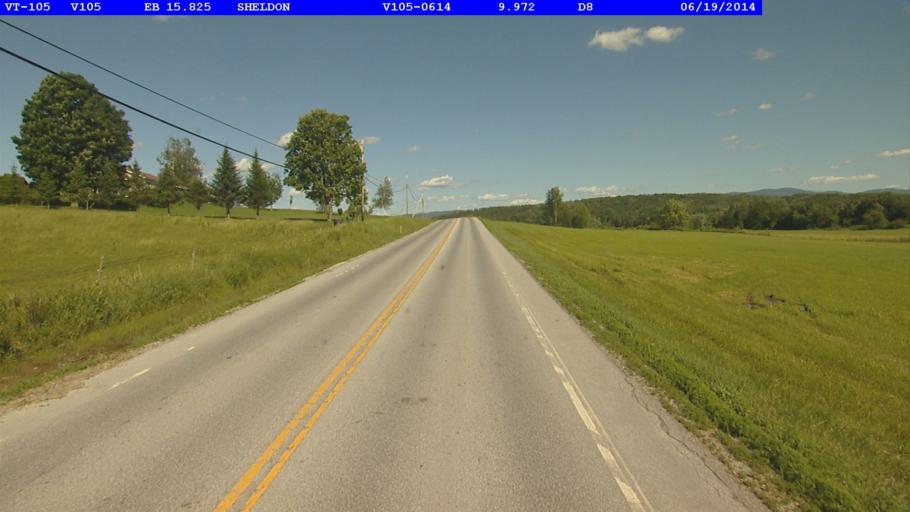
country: US
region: Vermont
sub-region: Franklin County
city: Enosburg Falls
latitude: 44.9081
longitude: -72.8406
